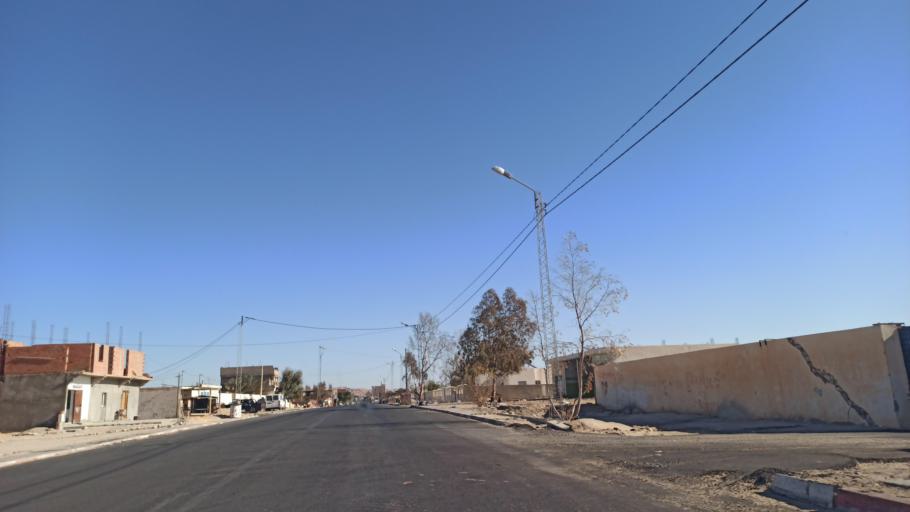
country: TN
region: Gafsa
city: Al Metlaoui
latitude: 34.3102
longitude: 8.3796
